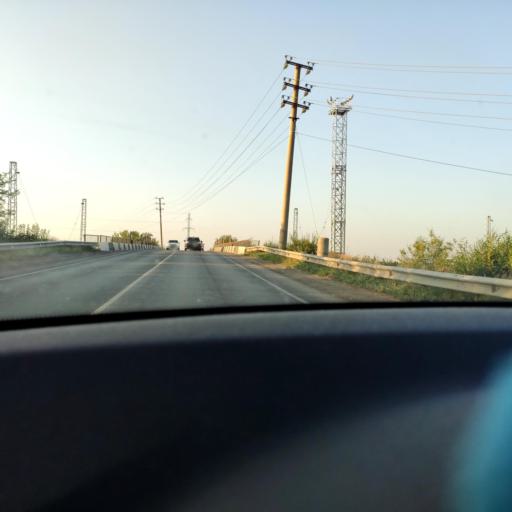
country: RU
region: Samara
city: Kinel'
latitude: 53.2415
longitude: 50.5817
